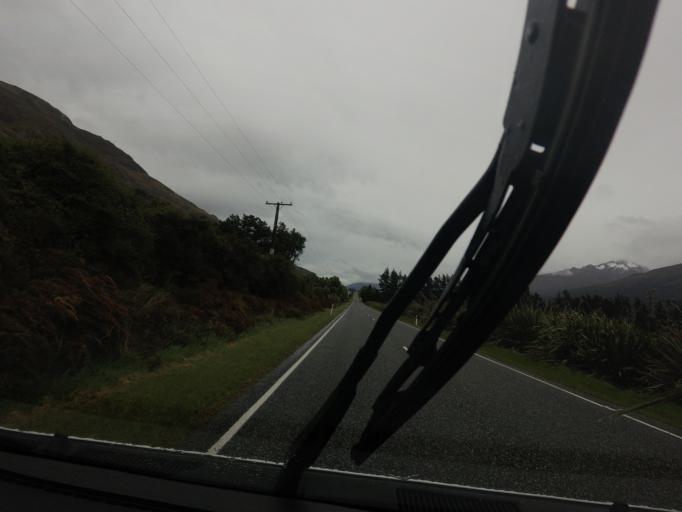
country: NZ
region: Otago
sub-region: Queenstown-Lakes District
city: Wanaka
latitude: -44.2870
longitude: 169.2014
